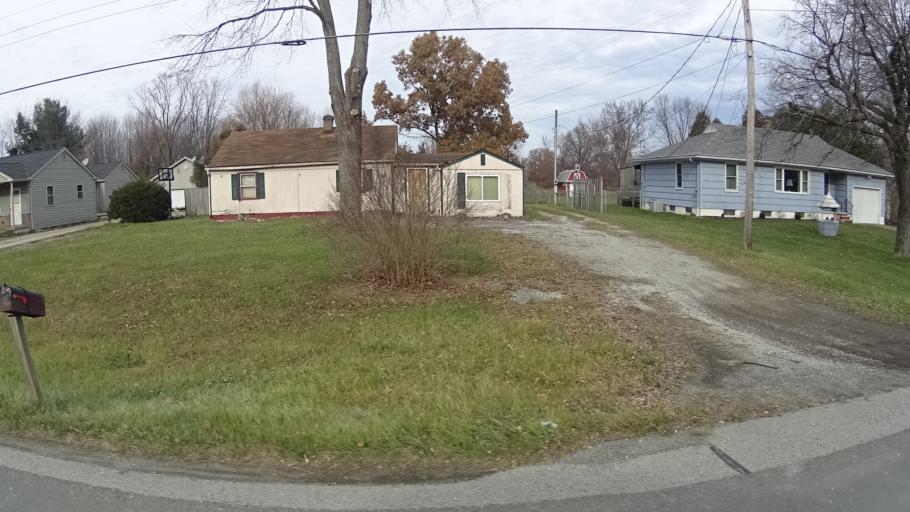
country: US
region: Ohio
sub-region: Lorain County
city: Eaton Estates
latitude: 41.3131
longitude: -81.9515
